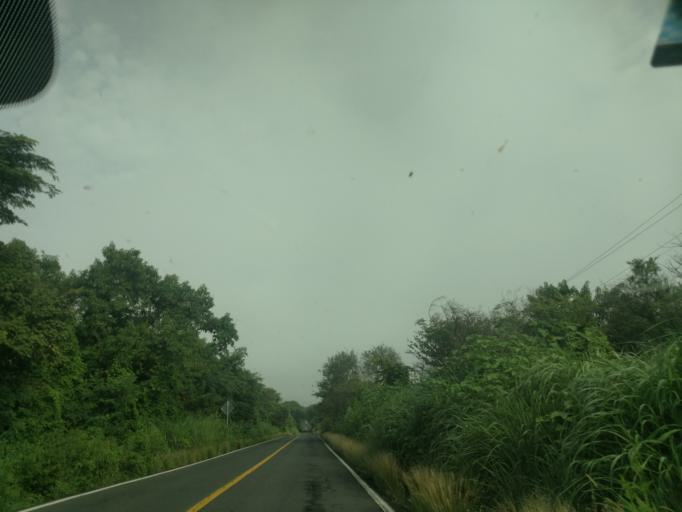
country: MX
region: Jalisco
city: Ameca
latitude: 20.5330
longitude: -104.1349
